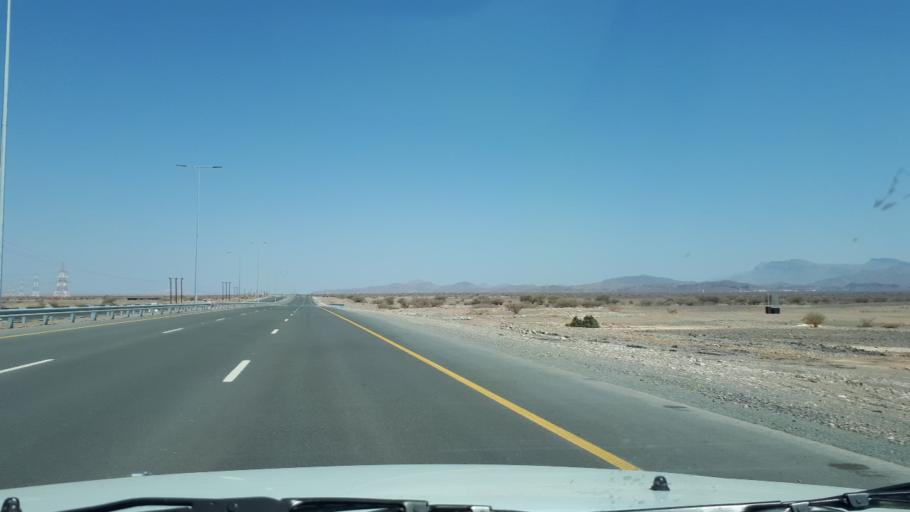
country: OM
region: Ash Sharqiyah
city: Badiyah
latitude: 22.4076
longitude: 59.0604
